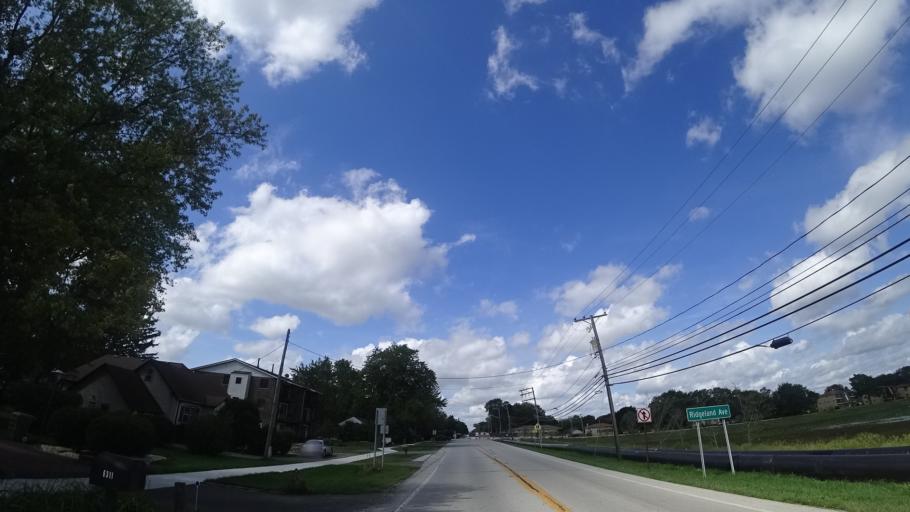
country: US
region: Illinois
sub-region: Cook County
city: Tinley Park
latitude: 41.5734
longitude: -87.7728
